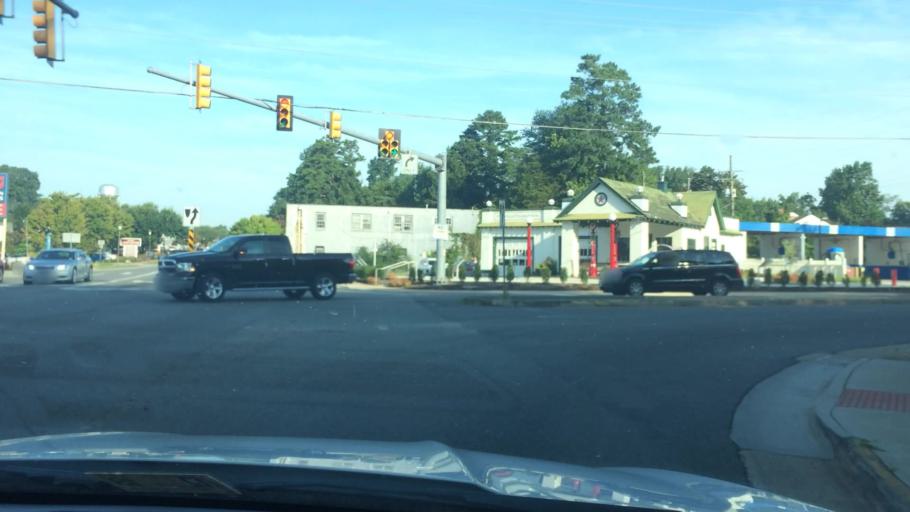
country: US
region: Virginia
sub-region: Gloucester County
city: Gloucester Courthouse
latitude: 37.4122
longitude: -76.5200
